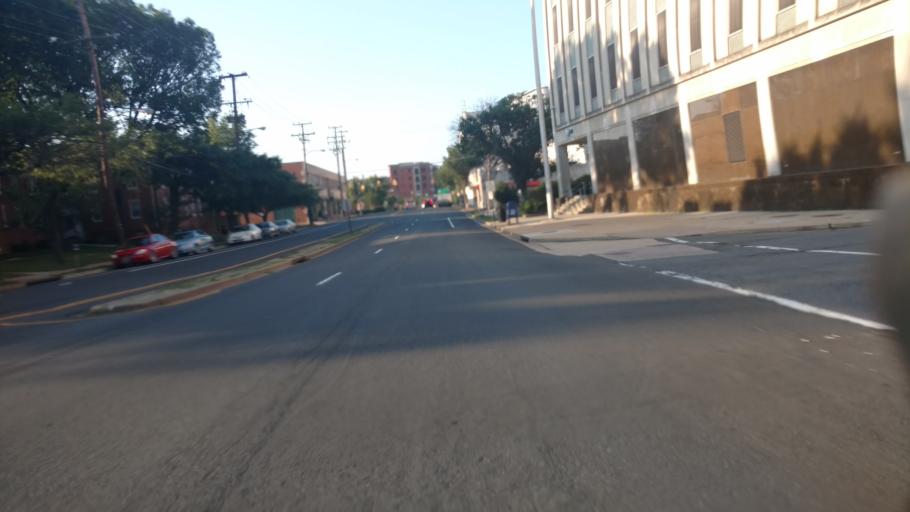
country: US
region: Virginia
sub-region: Arlington County
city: Arlington
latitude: 38.8641
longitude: -77.0874
